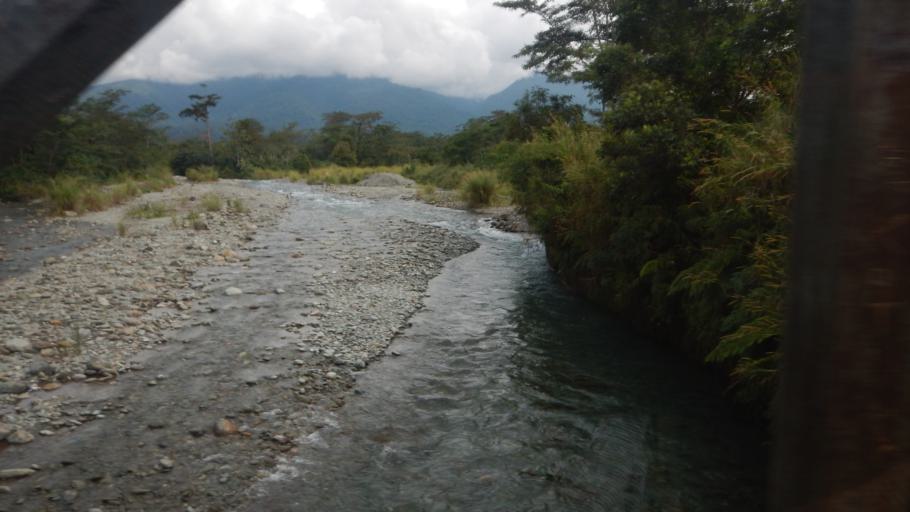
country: PG
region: Northern Province
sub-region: Sohe
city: Kokoda
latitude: -8.9200
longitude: 147.9470
